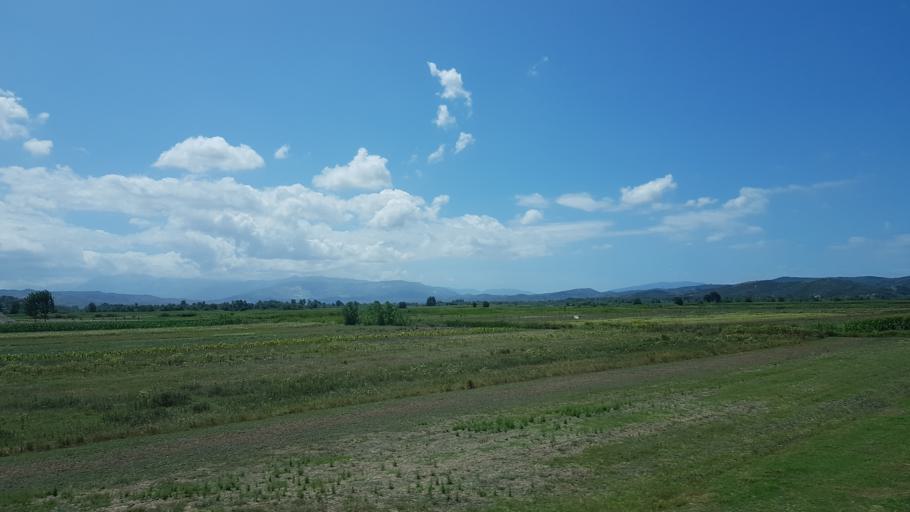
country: AL
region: Fier
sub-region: Rrethi i Fierit
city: Cakran
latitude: 40.5946
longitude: 19.5745
